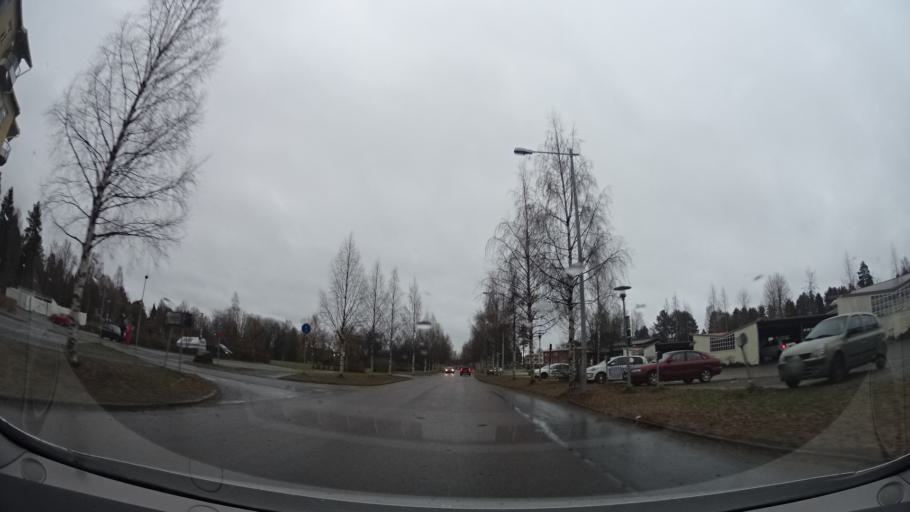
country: SE
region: Vaesterbotten
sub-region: Skelleftea Kommun
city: Skelleftea
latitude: 64.7604
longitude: 20.9541
